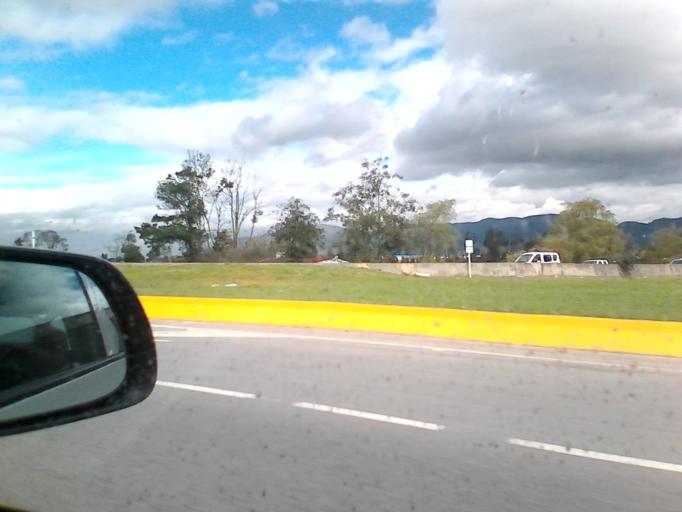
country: CO
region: Cundinamarca
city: Chia
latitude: 4.8548
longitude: -74.0296
